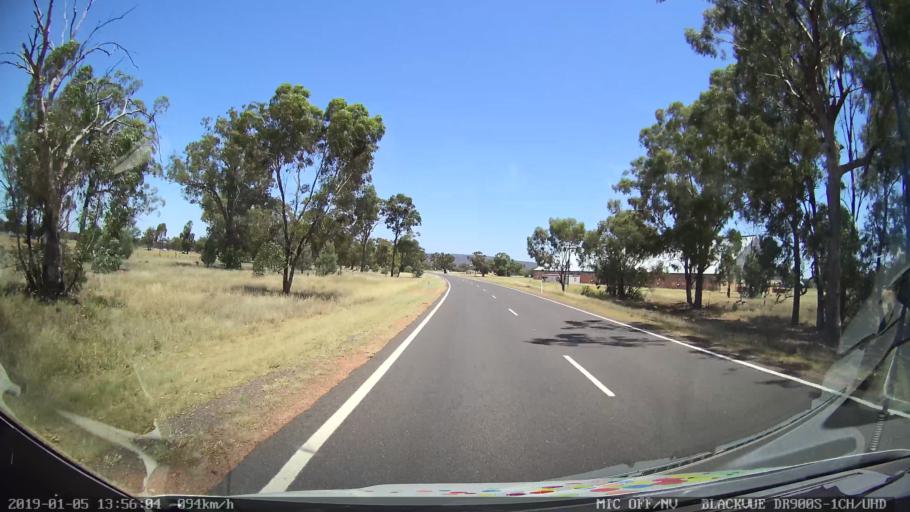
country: AU
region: New South Wales
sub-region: Gunnedah
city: Gunnedah
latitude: -31.1119
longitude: 150.2699
